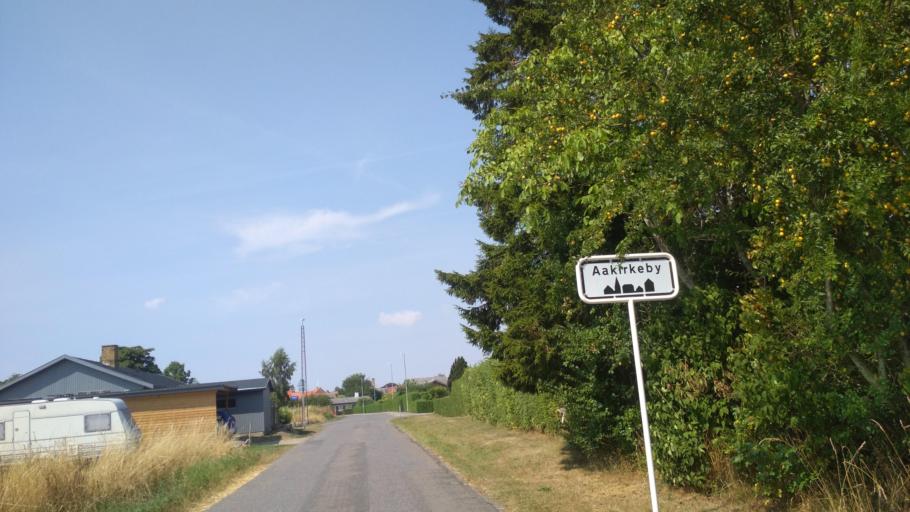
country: DK
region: Capital Region
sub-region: Bornholm Kommune
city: Akirkeby
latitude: 55.0676
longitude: 14.9291
